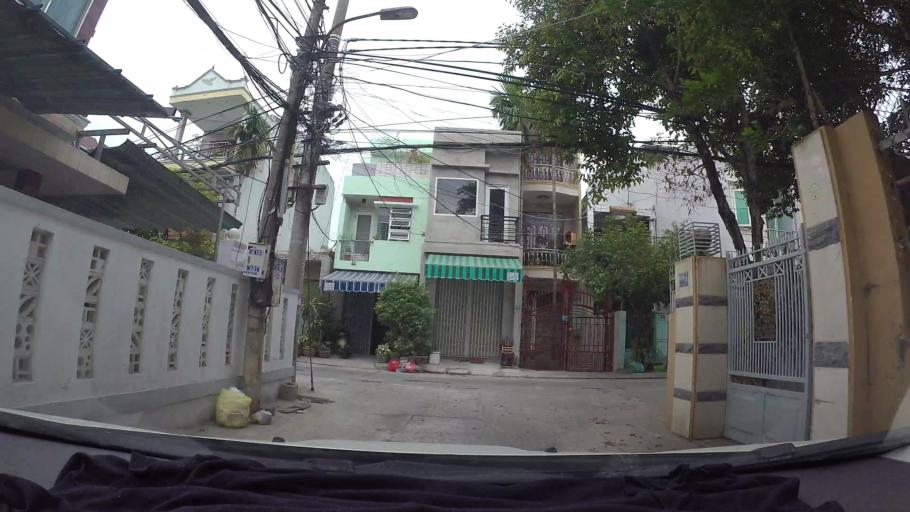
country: VN
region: Da Nang
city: Thanh Khe
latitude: 16.0707
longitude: 108.1883
